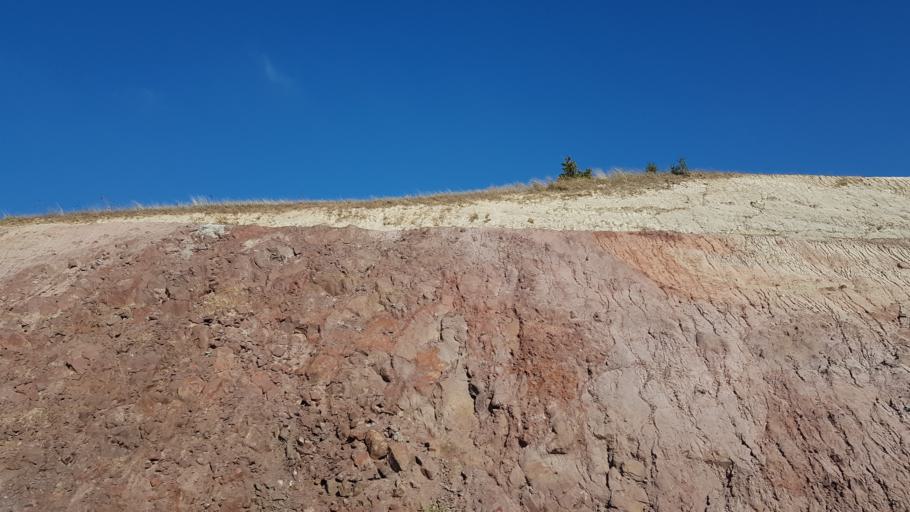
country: TR
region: Balikesir
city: Ertugrul
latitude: 39.5447
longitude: 27.6785
